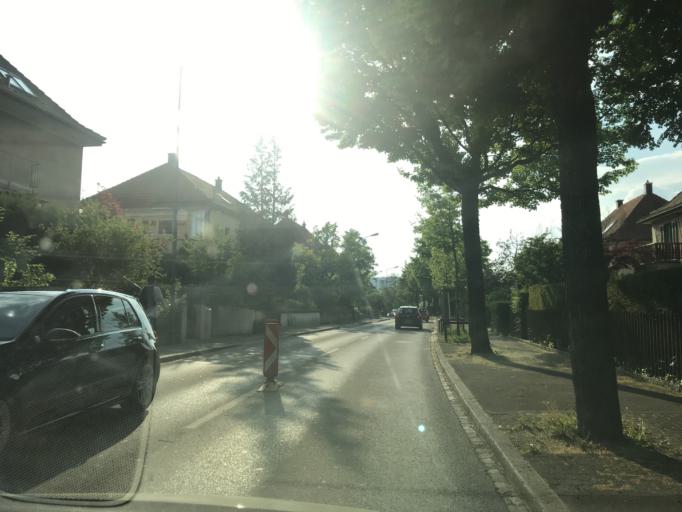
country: CH
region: Zurich
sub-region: Bezirk Winterthur
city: Stadt Winterthur (Kreis 1) / Heiligberg
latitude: 47.4903
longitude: 8.7242
